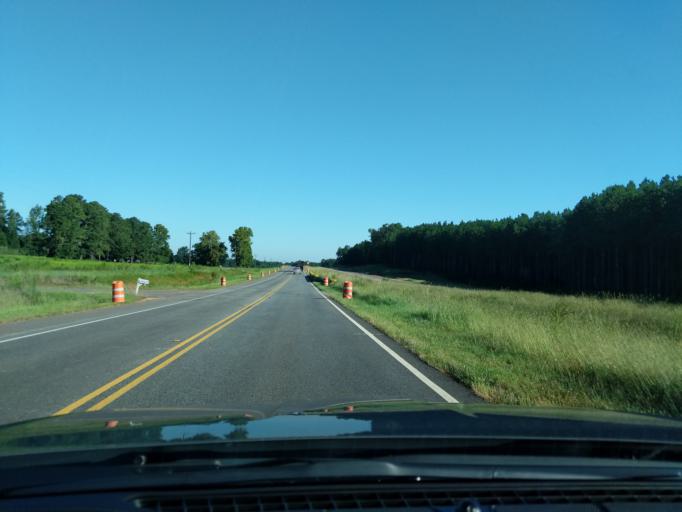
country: US
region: Georgia
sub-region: McDuffie County
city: Thomson
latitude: 33.5636
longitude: -82.5163
